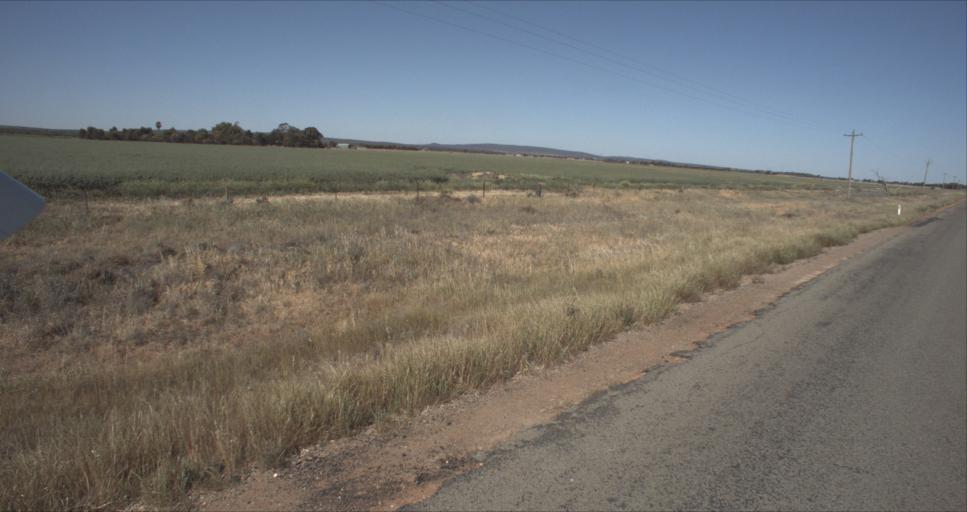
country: AU
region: New South Wales
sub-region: Leeton
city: Leeton
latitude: -34.4834
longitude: 146.3741
